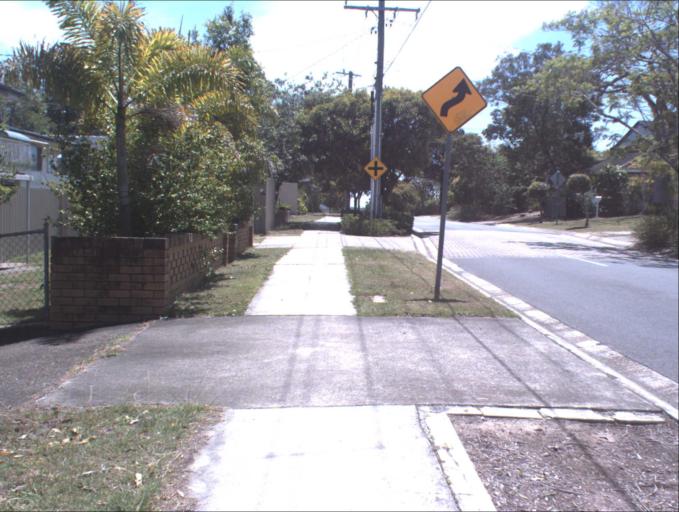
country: AU
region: Queensland
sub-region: Logan
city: Rochedale South
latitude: -27.5991
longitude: 153.1302
